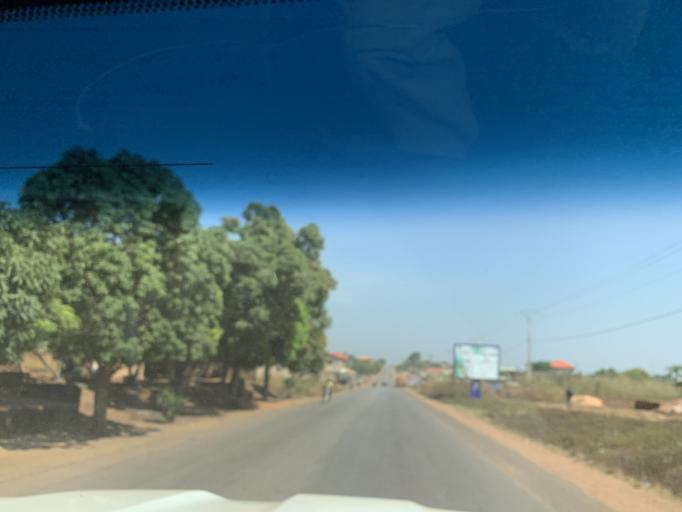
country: GN
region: Kindia
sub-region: Kindia
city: Kindia
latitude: 10.0221
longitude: -12.8794
